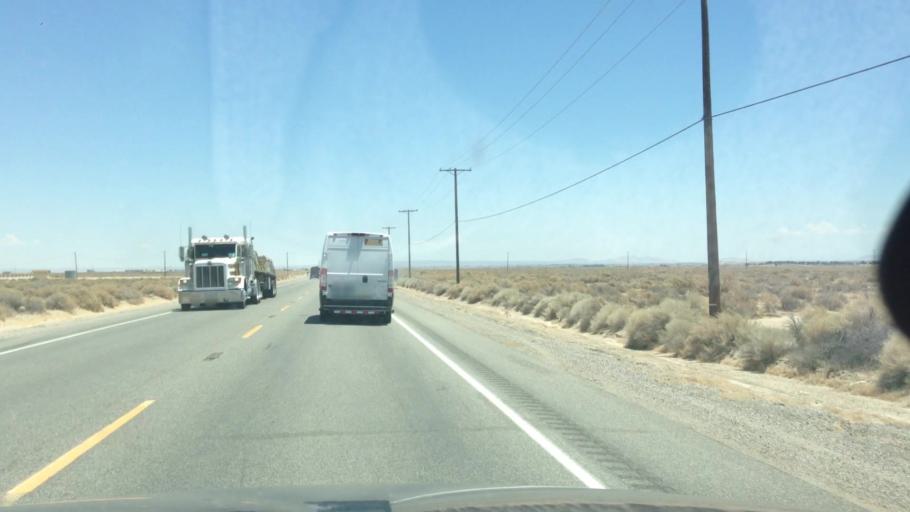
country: US
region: California
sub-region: Kern County
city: Rosamond
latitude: 34.7766
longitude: -118.2088
